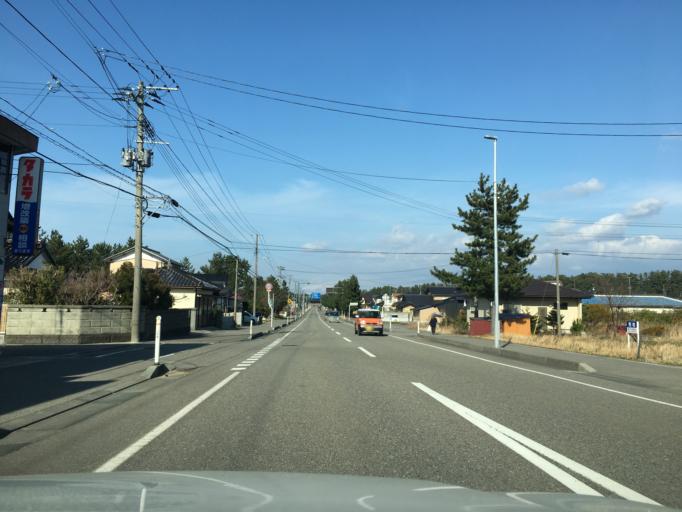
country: JP
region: Yamagata
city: Tsuruoka
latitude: 38.7874
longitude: 139.7653
